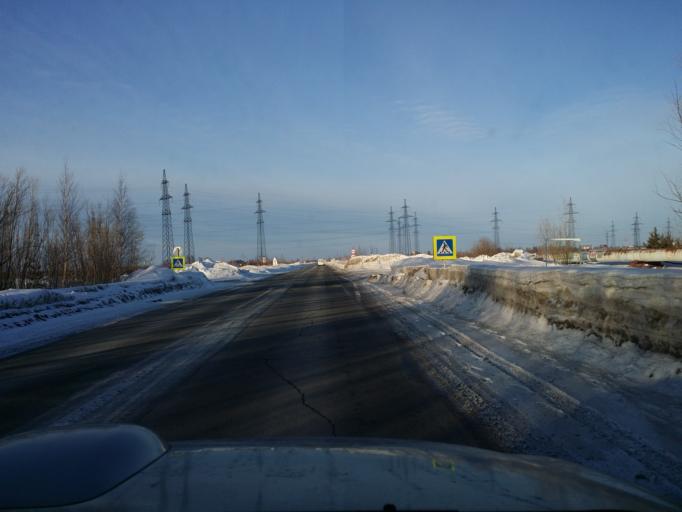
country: RU
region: Khanty-Mansiyskiy Avtonomnyy Okrug
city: Izluchinsk
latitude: 60.9663
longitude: 76.8848
